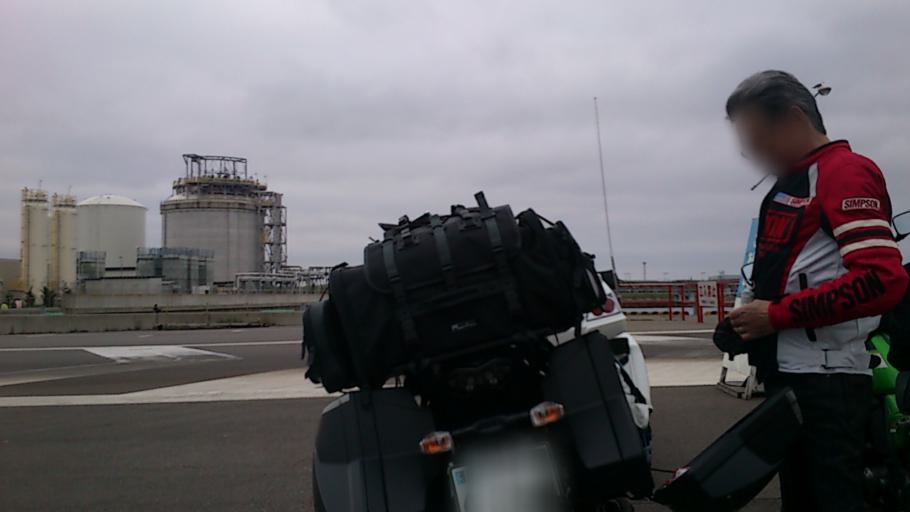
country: JP
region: Hokkaido
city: Hakodate
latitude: 41.8075
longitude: 140.7112
